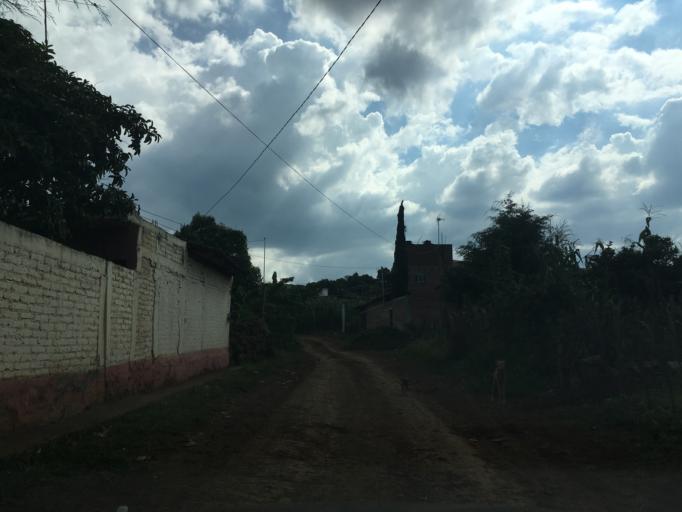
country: MX
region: Mexico
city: El Guayabito
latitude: 19.8997
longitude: -102.5002
